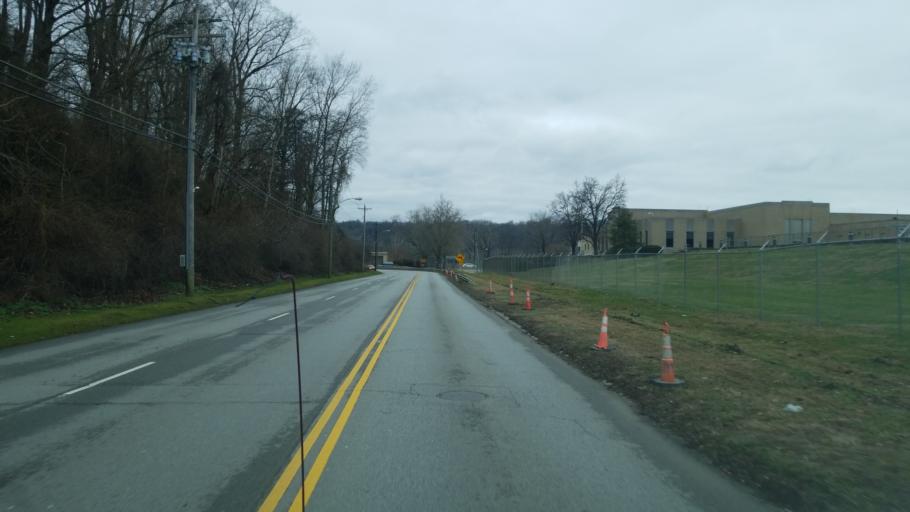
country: US
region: Kentucky
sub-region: Campbell County
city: Fort Thomas
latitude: 39.0724
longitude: -84.4212
